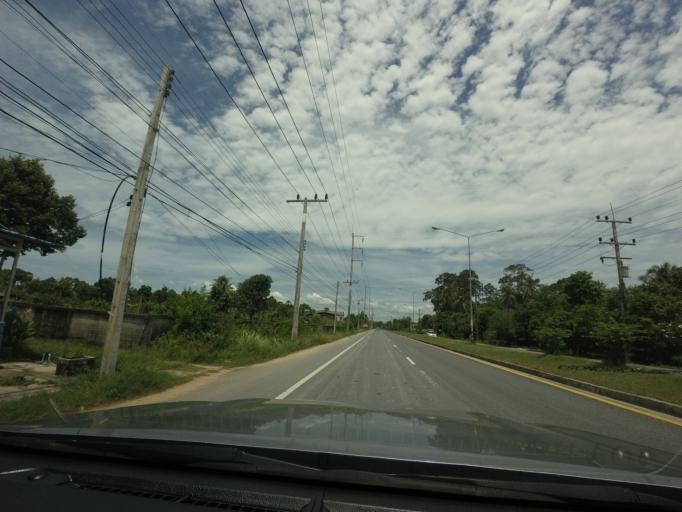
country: TH
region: Songkhla
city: Sathing Phra
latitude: 7.5566
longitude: 100.4139
